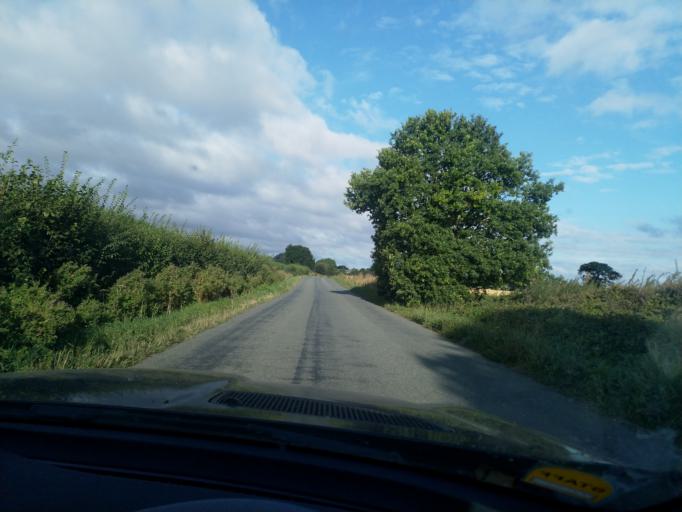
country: GB
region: England
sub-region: Suffolk
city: Elmswell
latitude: 52.2338
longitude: 0.9594
